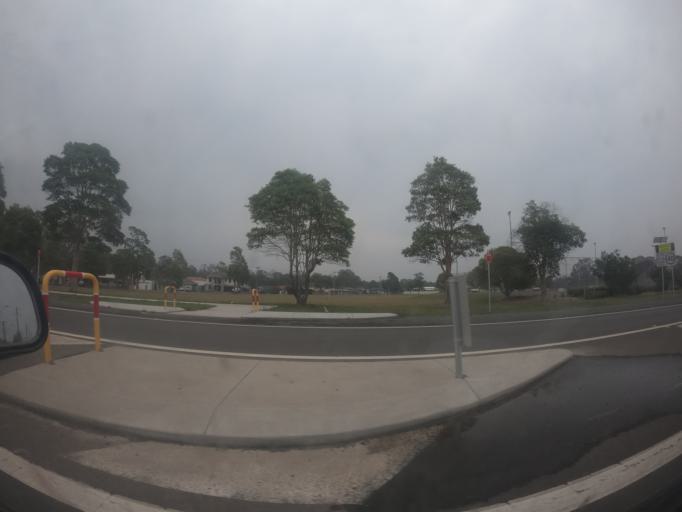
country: AU
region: New South Wales
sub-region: Shellharbour
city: Albion Park Rail
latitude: -34.5691
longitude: 150.7950
